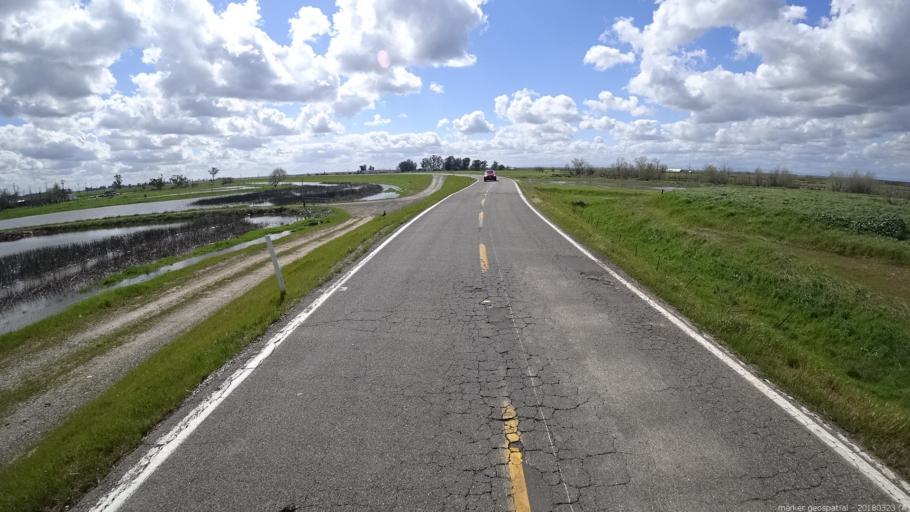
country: US
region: California
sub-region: Sacramento County
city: Elverta
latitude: 38.7341
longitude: -121.4909
